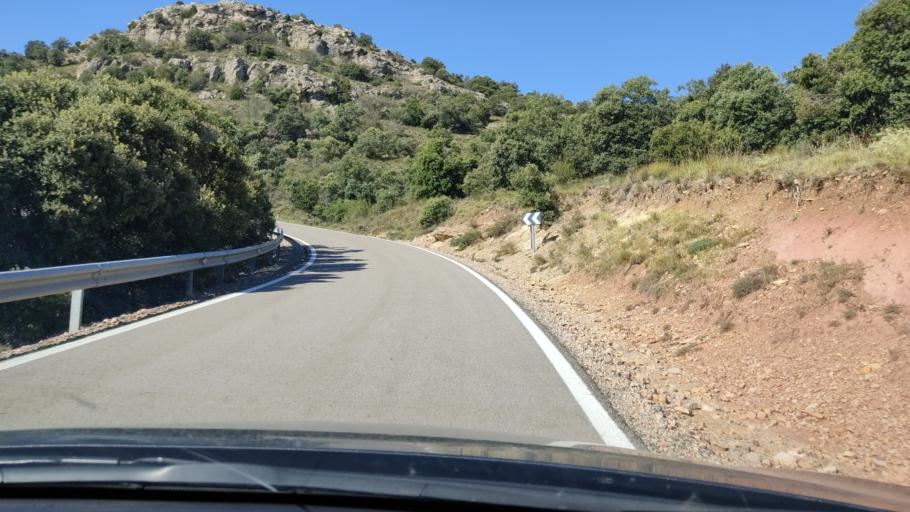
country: ES
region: Aragon
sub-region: Provincia de Teruel
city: Anadon
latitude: 41.0010
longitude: -1.0034
